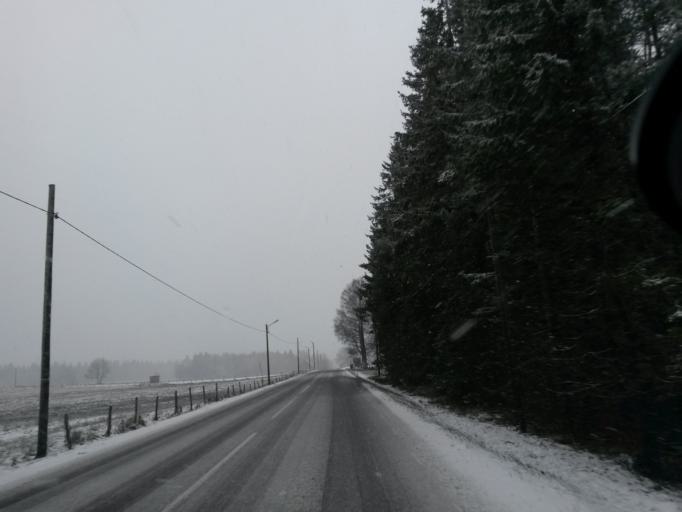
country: SE
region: Vaestra Goetaland
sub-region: Boras Kommun
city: Ganghester
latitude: 57.7574
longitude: 13.0143
